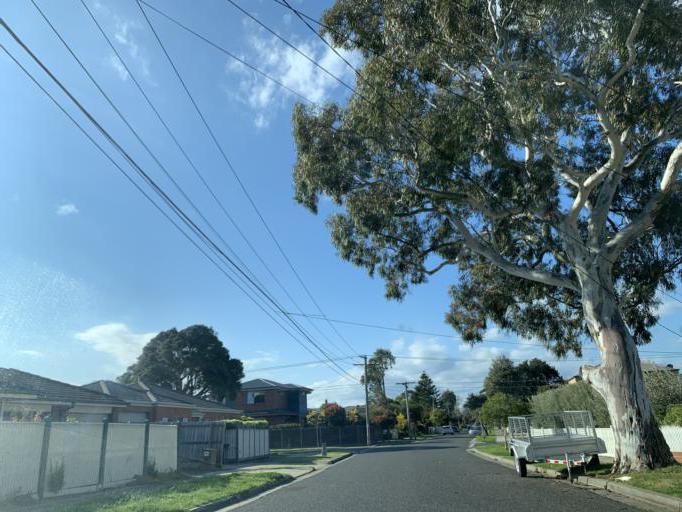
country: AU
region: Victoria
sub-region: Kingston
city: Mordialloc
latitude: -37.9981
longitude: 145.0940
